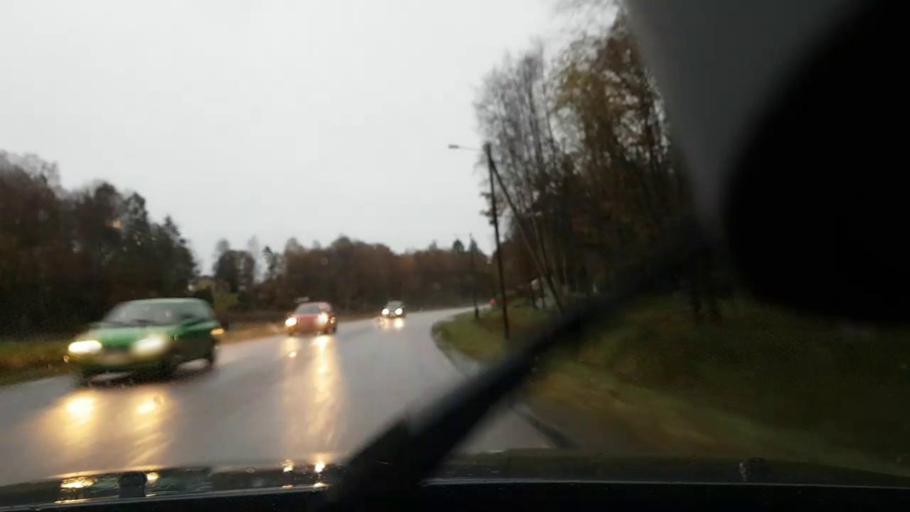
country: SE
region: Vaestra Goetaland
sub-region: Molndal
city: Lindome
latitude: 57.5919
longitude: 12.0907
